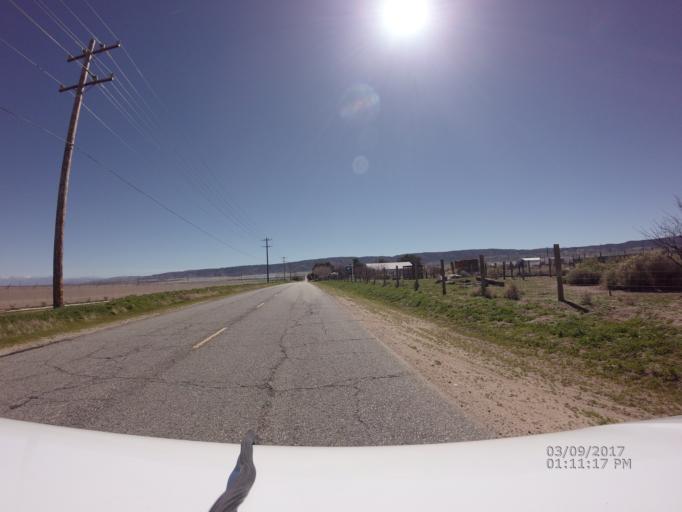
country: US
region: California
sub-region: Los Angeles County
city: Leona Valley
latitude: 34.6928
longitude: -118.2893
